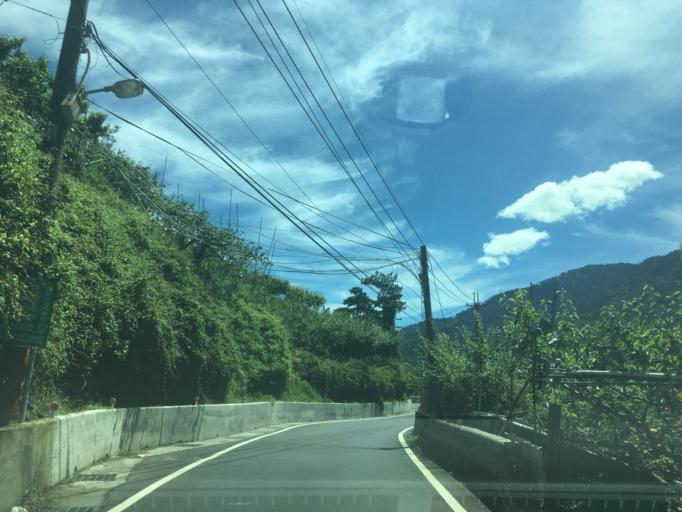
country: TW
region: Taiwan
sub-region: Nantou
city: Puli
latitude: 24.2544
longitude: 121.2604
